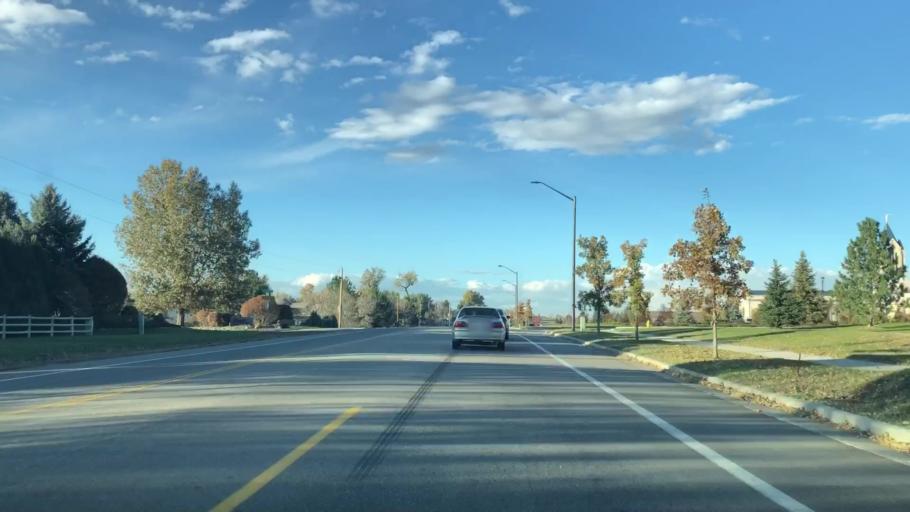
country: US
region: Colorado
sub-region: Larimer County
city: Loveland
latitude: 40.4918
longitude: -105.0393
